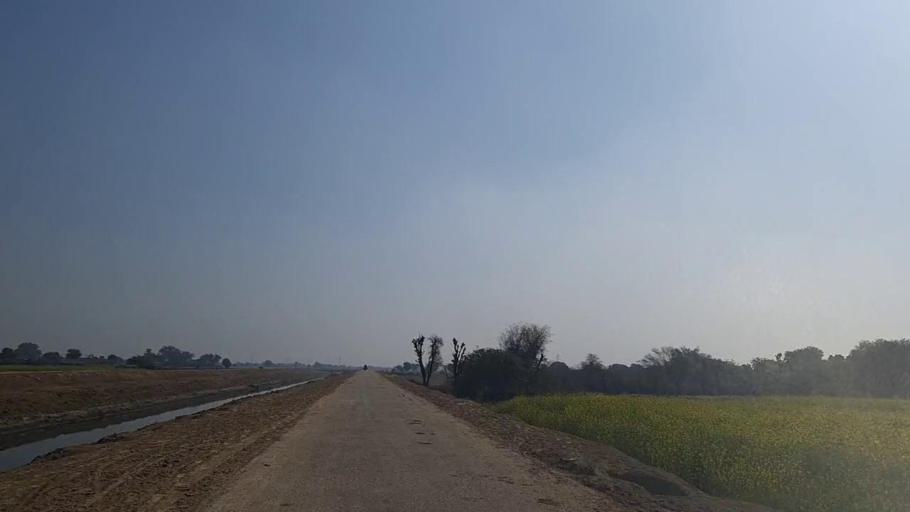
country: PK
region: Sindh
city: Shahpur Chakar
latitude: 26.1800
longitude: 68.5682
